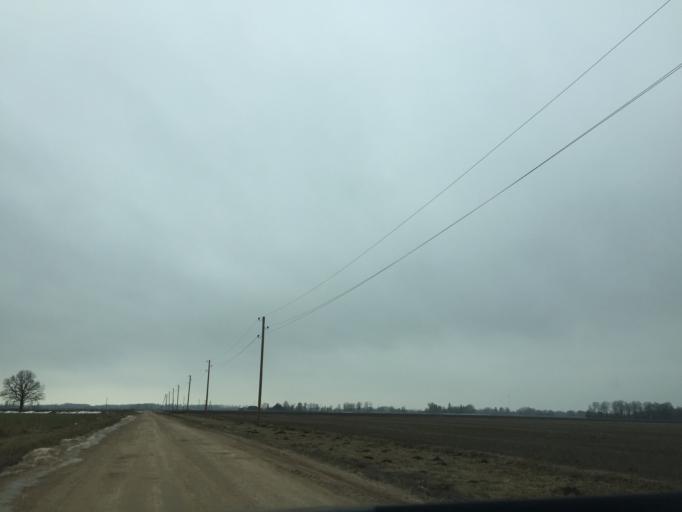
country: LV
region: Rundales
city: Pilsrundale
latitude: 56.5610
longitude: 24.0341
